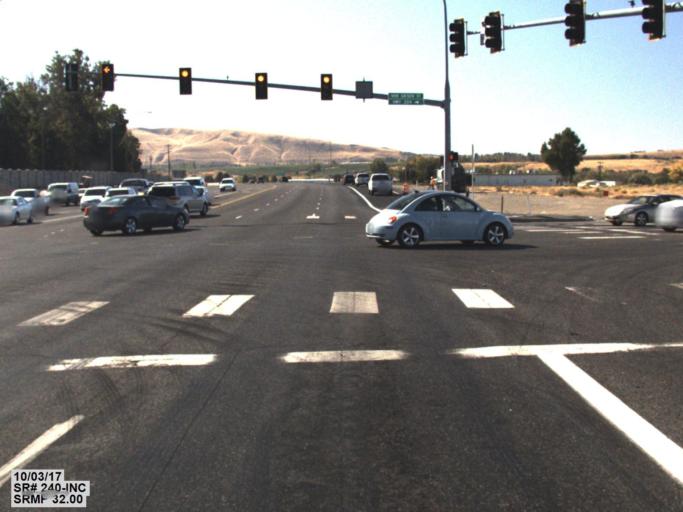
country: US
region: Washington
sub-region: Benton County
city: Richland
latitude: 46.2934
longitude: -119.3046
